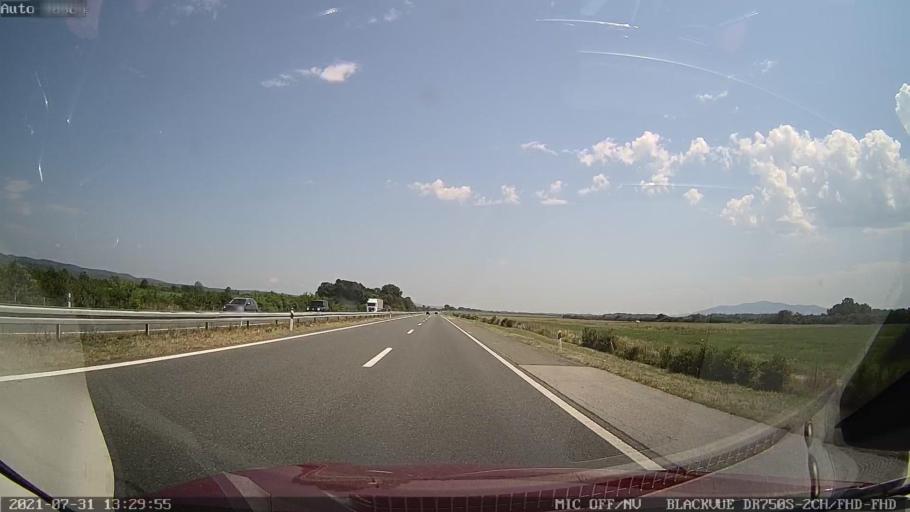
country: HR
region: Brodsko-Posavska
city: Vrbova
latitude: 45.2151
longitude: 17.5241
